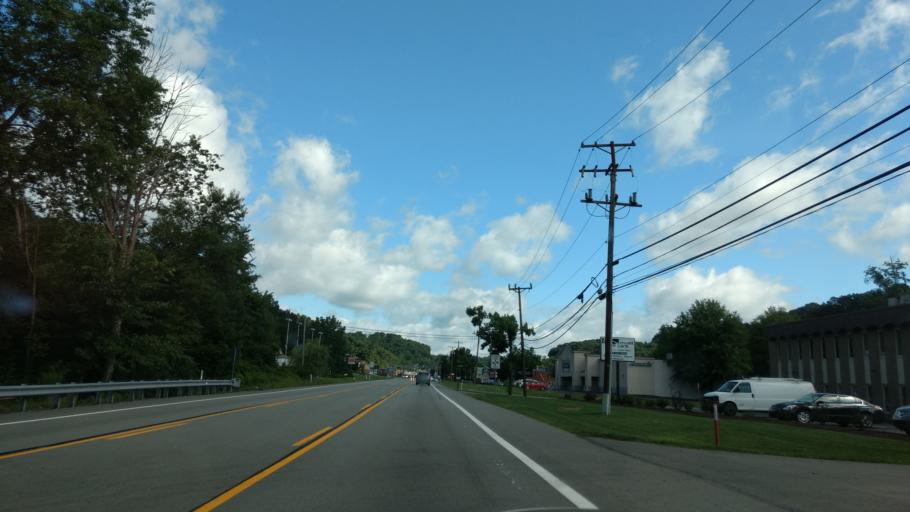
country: US
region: Pennsylvania
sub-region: Westmoreland County
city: Murrysville
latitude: 40.4389
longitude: -79.7128
